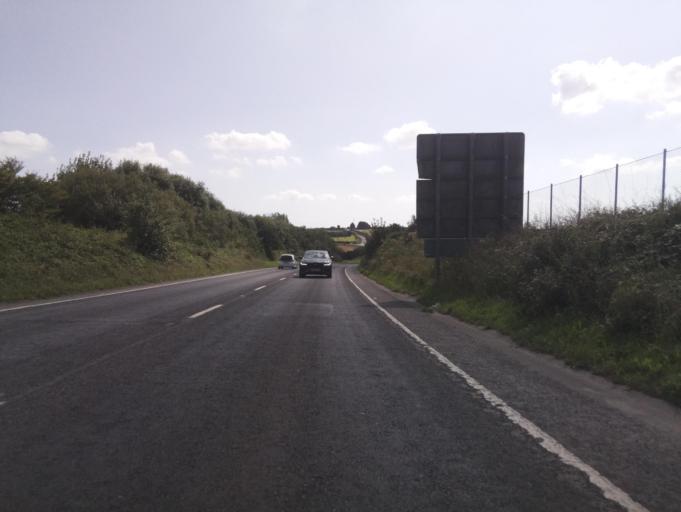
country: GB
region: England
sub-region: Cornwall
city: Saltash
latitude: 50.4350
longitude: -4.2565
